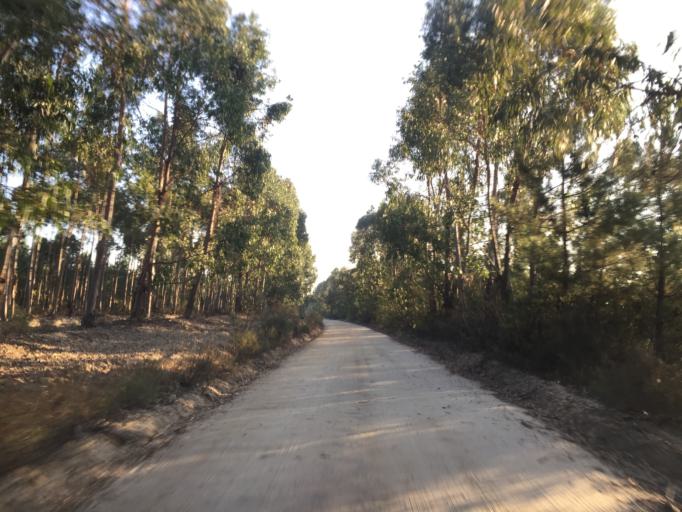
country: PT
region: Portalegre
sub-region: Ponte de Sor
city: Santo Andre
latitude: 39.1332
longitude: -8.3185
